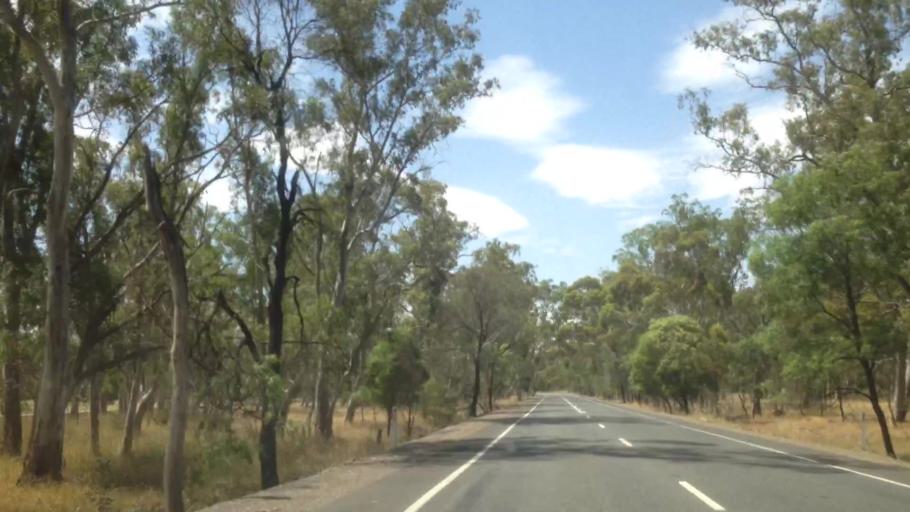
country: AU
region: South Australia
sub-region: Adelaide Hills
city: Birdwood
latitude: -34.7368
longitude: 138.9618
